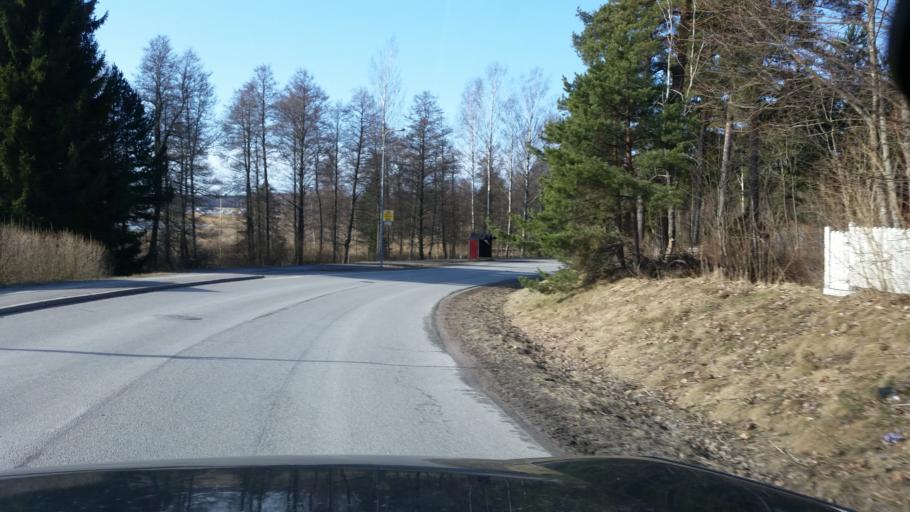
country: FI
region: Uusimaa
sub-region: Raaseporin
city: Inga
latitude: 60.0481
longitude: 24.0151
